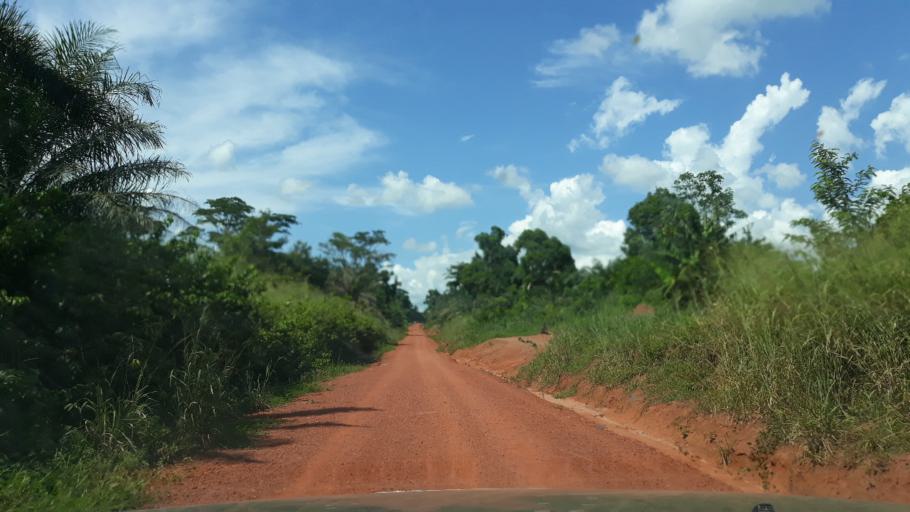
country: CD
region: Equateur
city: Businga
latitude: 3.4069
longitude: 20.3933
